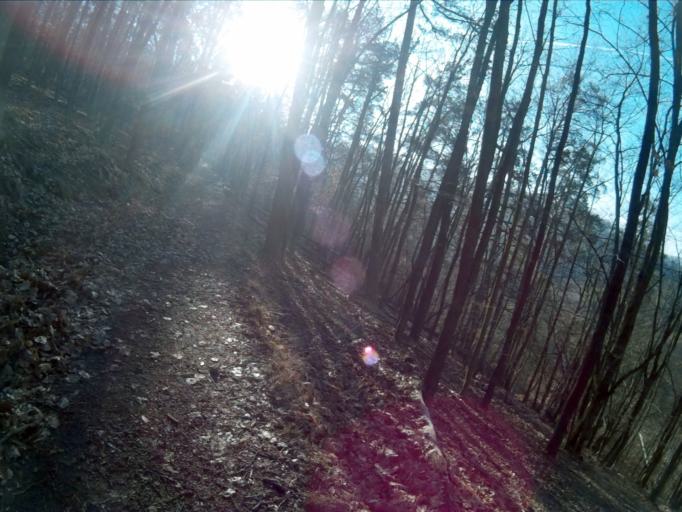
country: CZ
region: Vysocina
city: Namest' nad Oslavou
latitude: 49.1677
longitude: 16.1737
